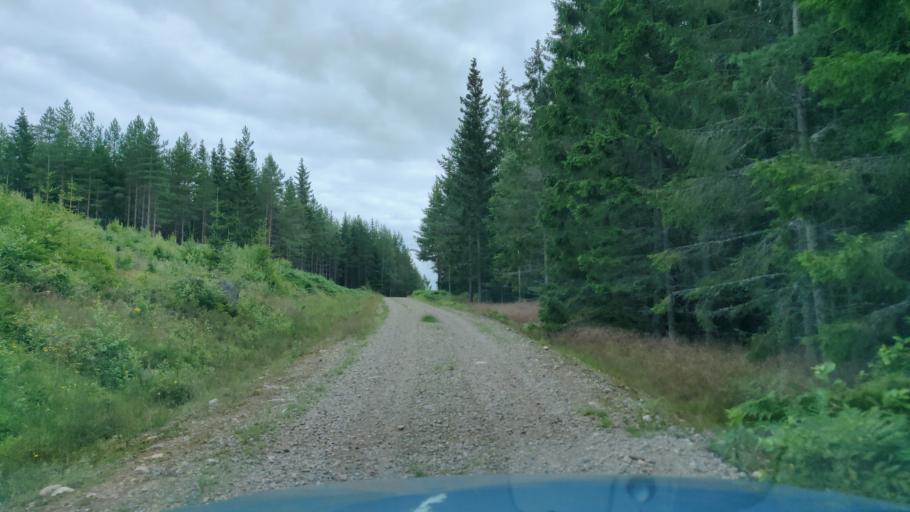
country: SE
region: Vaermland
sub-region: Hagfors Kommun
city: Hagfors
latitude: 59.9678
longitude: 13.5827
